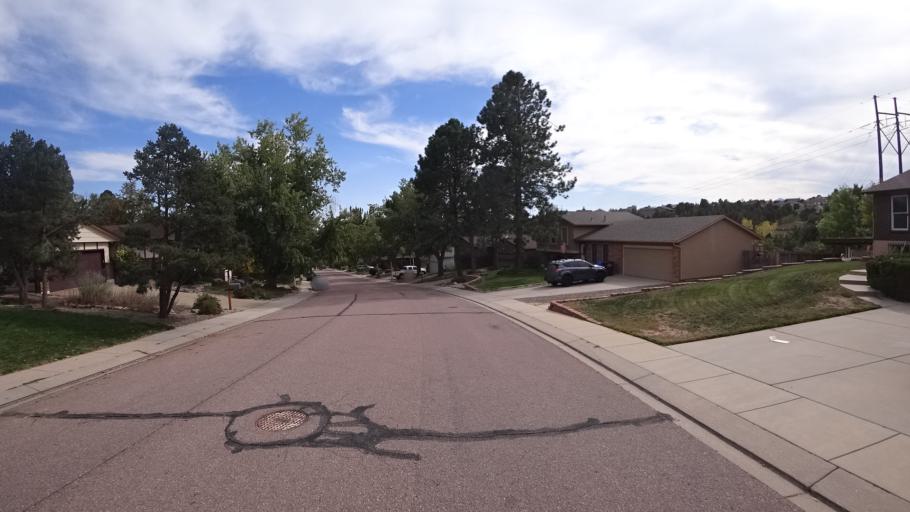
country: US
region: Colorado
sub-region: El Paso County
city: Colorado Springs
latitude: 38.9030
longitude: -104.7841
